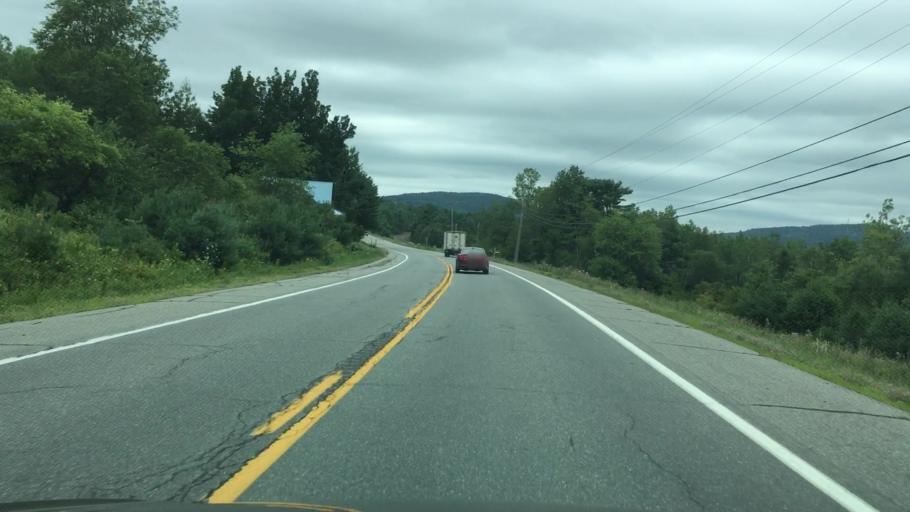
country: US
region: Maine
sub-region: Waldo County
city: Stockton Springs
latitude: 44.5382
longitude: -68.8611
